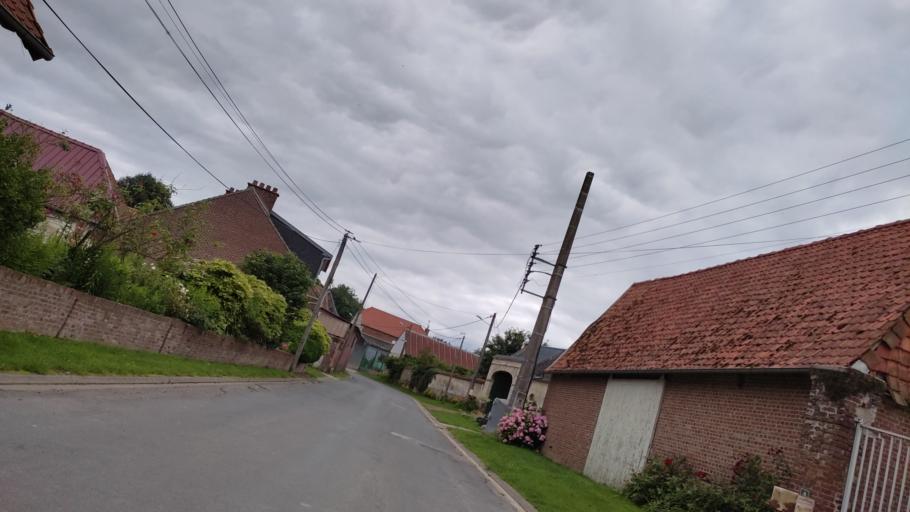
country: FR
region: Nord-Pas-de-Calais
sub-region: Departement du Pas-de-Calais
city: Beaumetz-les-Loges
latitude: 50.2409
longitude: 2.6279
